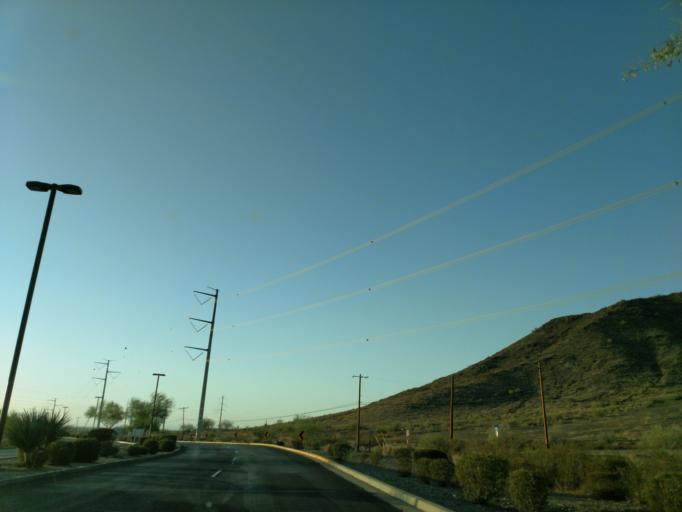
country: US
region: Arizona
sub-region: Maricopa County
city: Laveen
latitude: 33.3187
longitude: -112.1631
